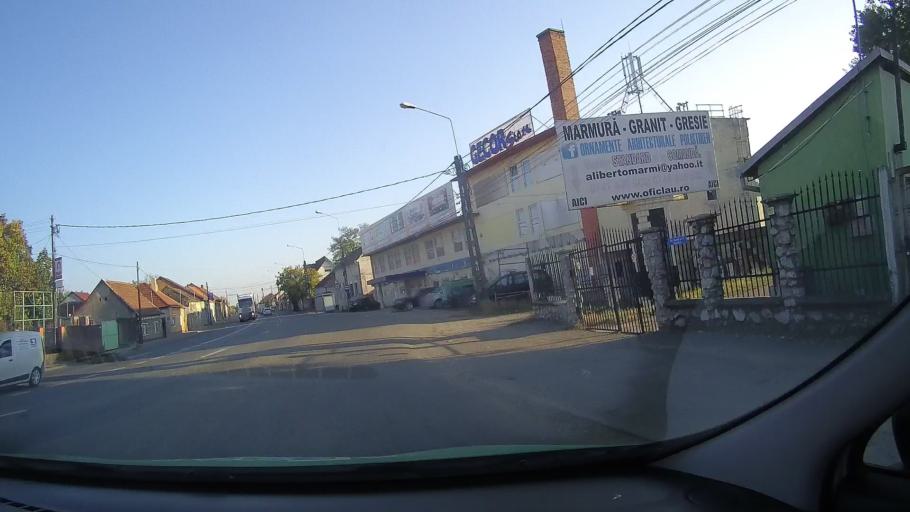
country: RO
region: Bihor
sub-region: Comuna Biharea
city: Oradea
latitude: 47.0963
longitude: 21.9014
